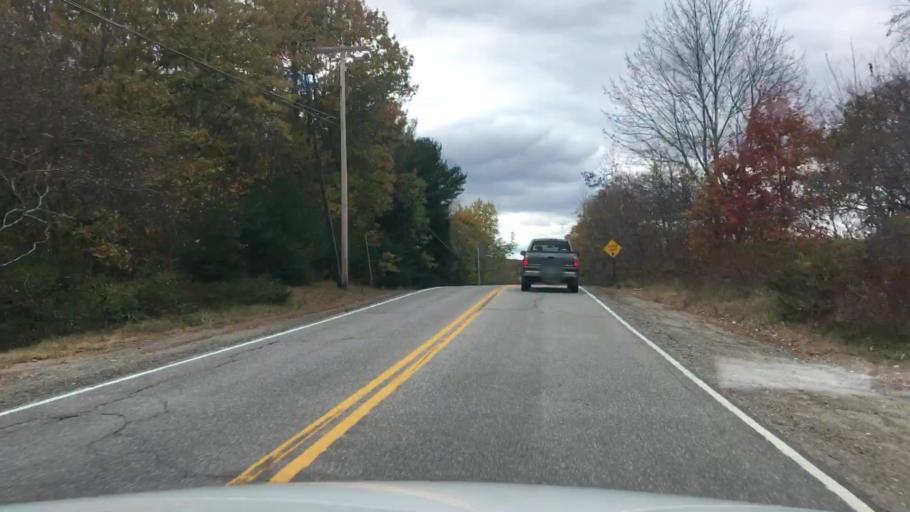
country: US
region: Maine
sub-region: Androscoggin County
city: Sabattus
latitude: 44.1352
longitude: -69.9993
